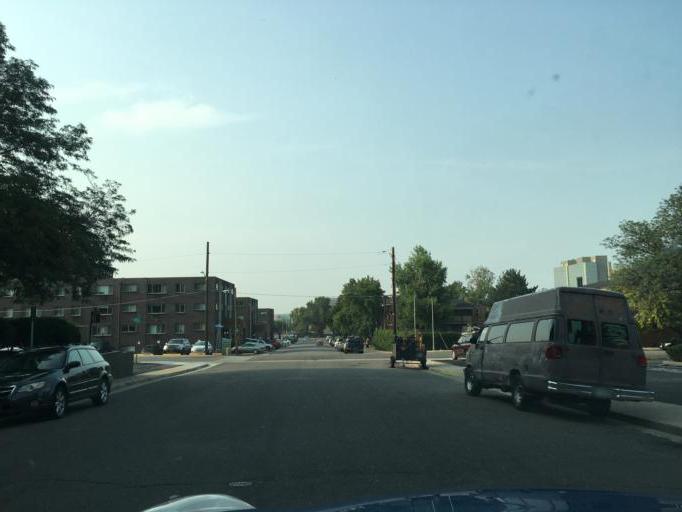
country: US
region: Colorado
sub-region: Arapahoe County
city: Glendale
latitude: 39.6942
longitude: -104.9363
